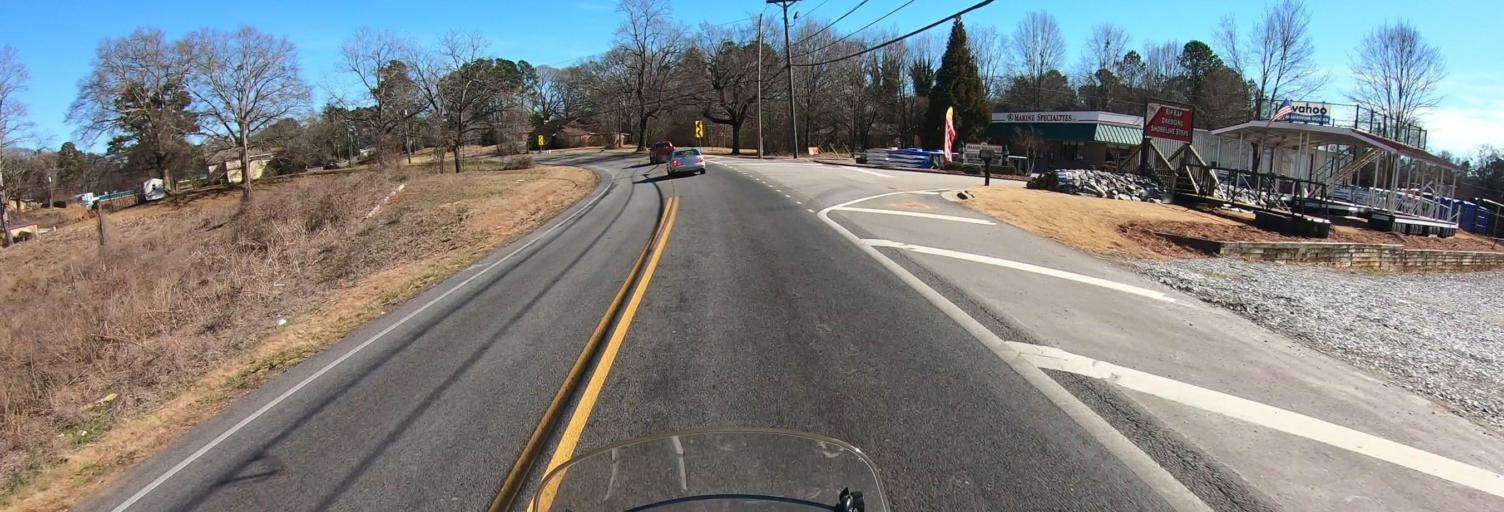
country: US
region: Georgia
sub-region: Hall County
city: Oakwood
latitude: 34.2735
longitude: -83.9108
